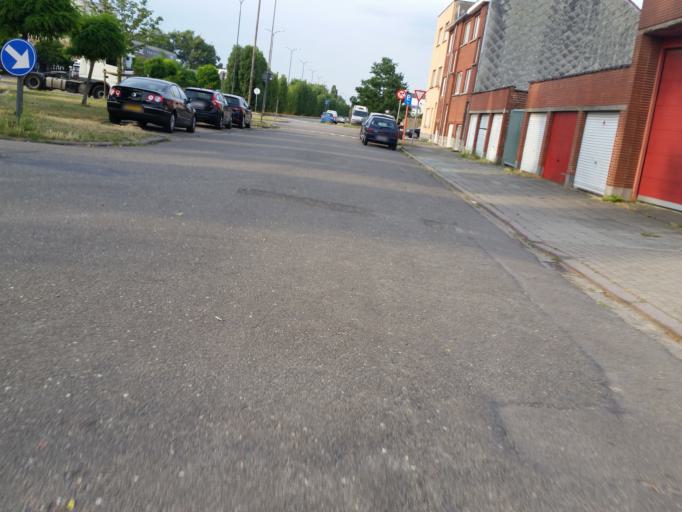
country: BE
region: Flanders
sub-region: Provincie Vlaams-Brabant
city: Vilvoorde
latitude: 50.9345
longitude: 4.4249
